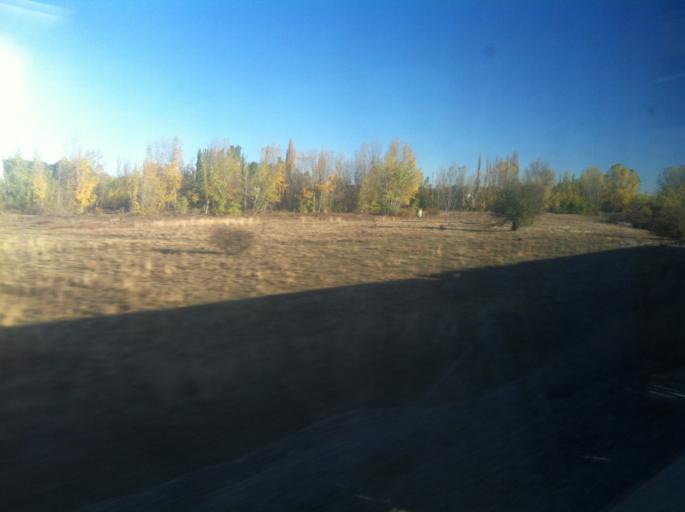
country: ES
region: Castille and Leon
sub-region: Provincia de Valladolid
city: Cubillas de Santa Marta
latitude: 41.8003
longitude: -4.5865
